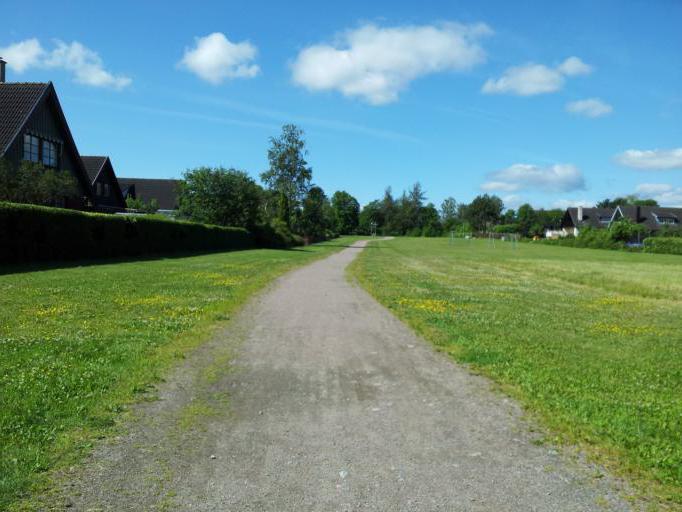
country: SE
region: Uppsala
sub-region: Uppsala Kommun
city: Saevja
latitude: 59.8692
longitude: 17.7031
